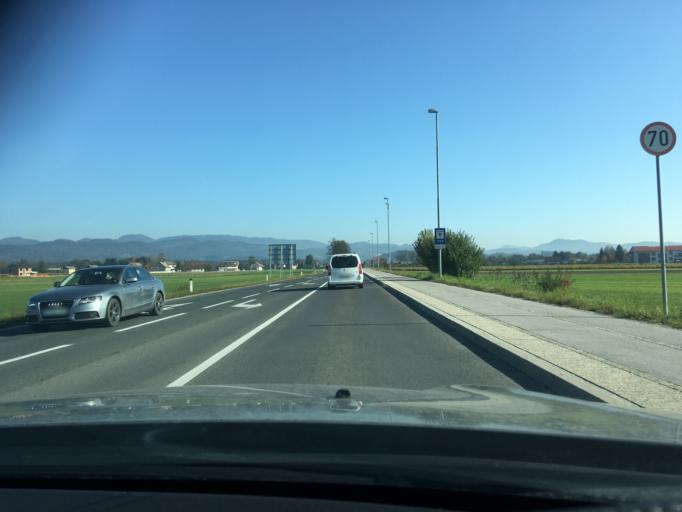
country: SI
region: Domzale
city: Vir
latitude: 46.1504
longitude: 14.6166
